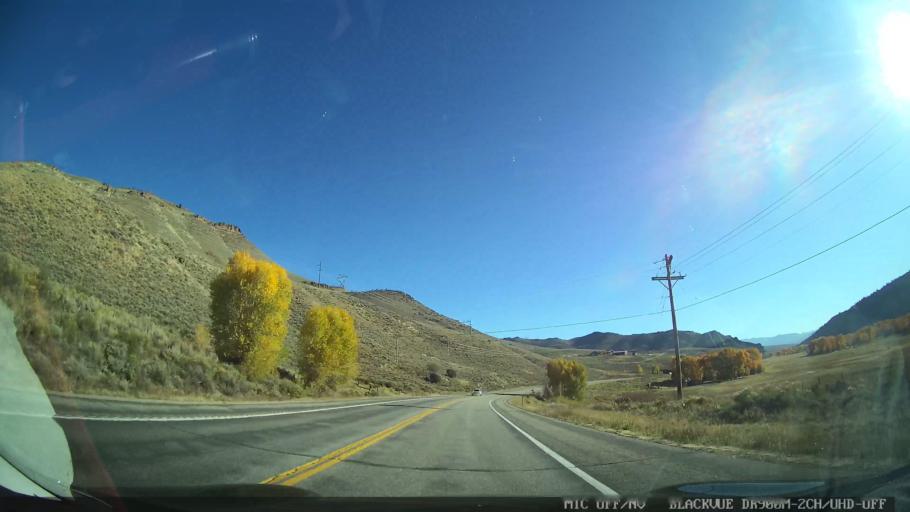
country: US
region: Colorado
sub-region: Grand County
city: Hot Sulphur Springs
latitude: 40.1060
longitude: -106.0251
